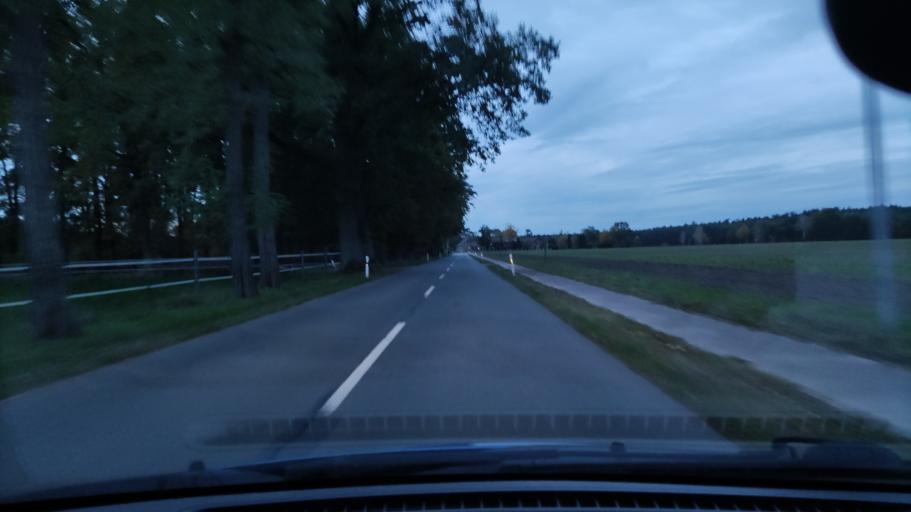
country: DE
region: Lower Saxony
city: Gorleben
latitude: 53.0442
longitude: 11.3863
